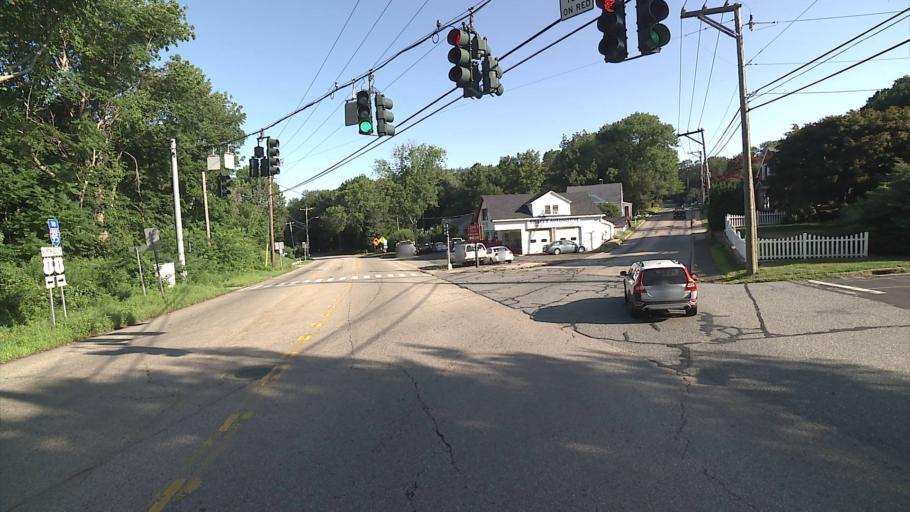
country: US
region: Connecticut
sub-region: New London County
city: Central Waterford
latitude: 41.3543
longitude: -72.1648
